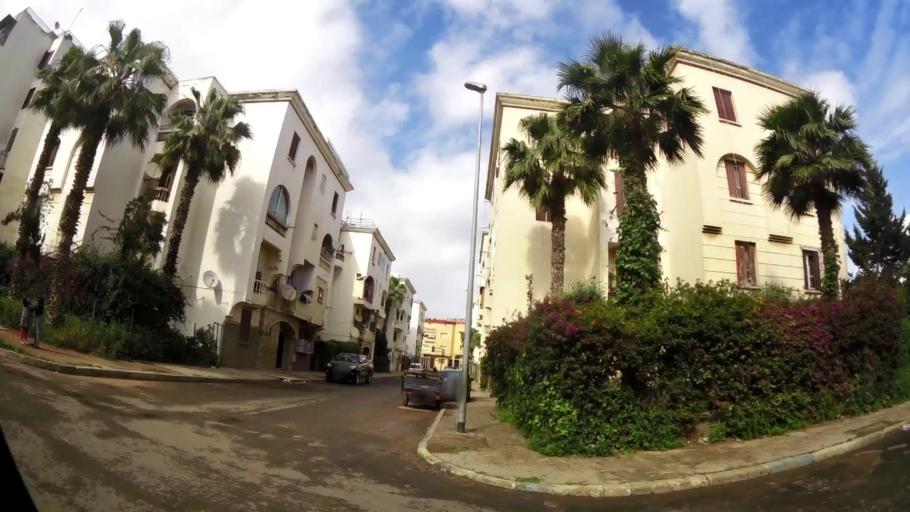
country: MA
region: Grand Casablanca
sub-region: Mohammedia
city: Mohammedia
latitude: 33.6758
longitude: -7.3834
